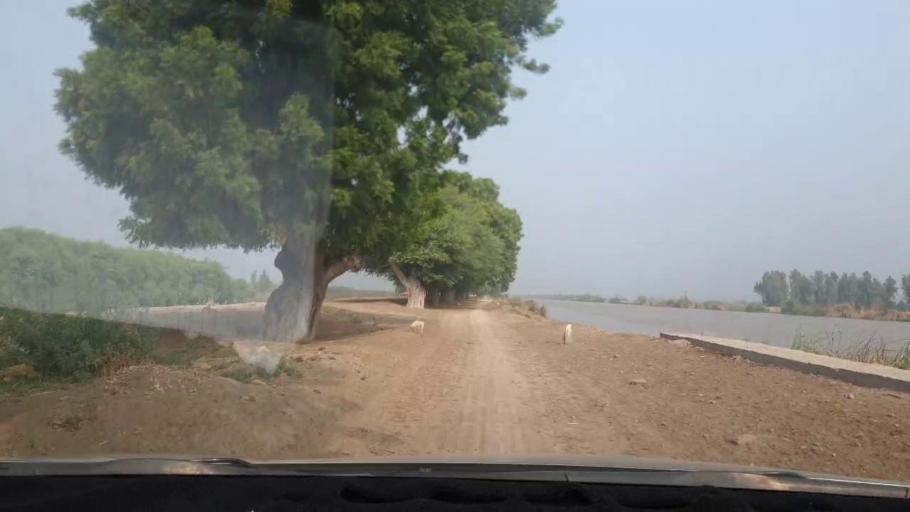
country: PK
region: Sindh
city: Matiari
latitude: 25.6739
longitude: 68.5578
